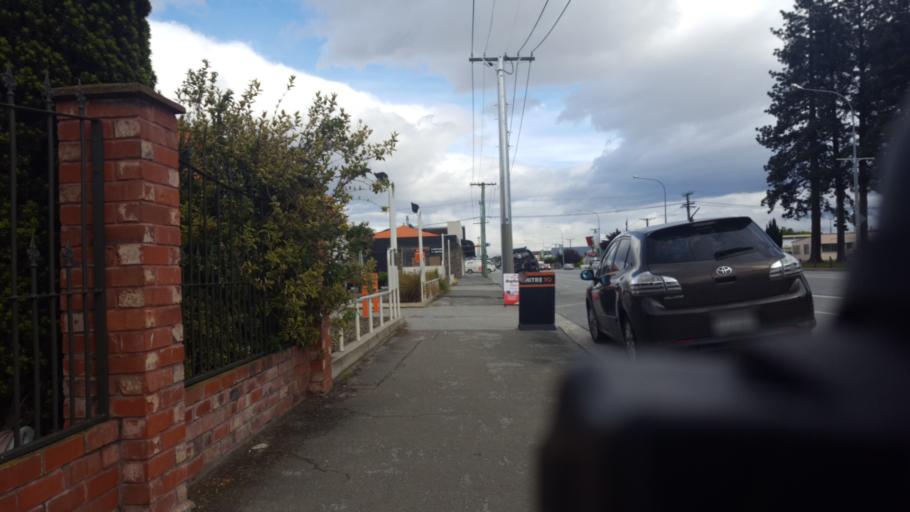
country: NZ
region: Otago
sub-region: Queenstown-Lakes District
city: Wanaka
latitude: -45.2542
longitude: 169.3911
